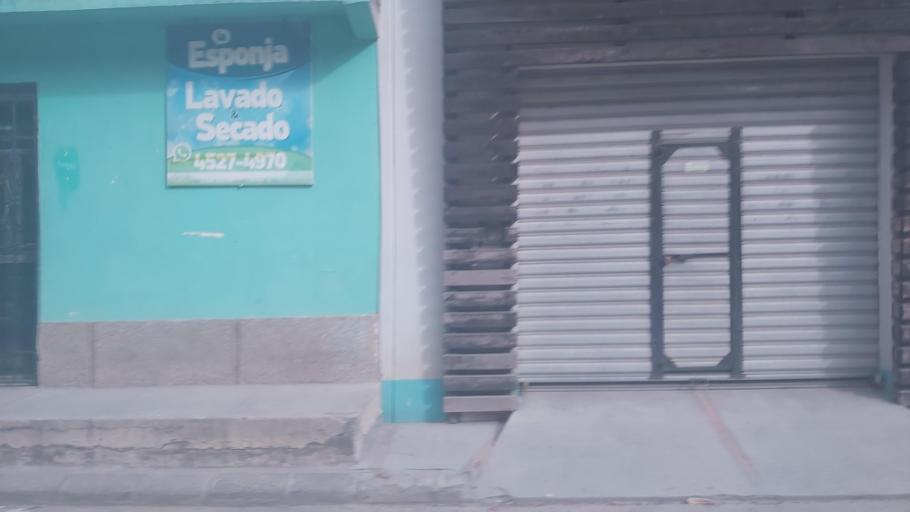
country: GT
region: Quetzaltenango
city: Quetzaltenango
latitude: 14.8286
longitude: -91.5285
